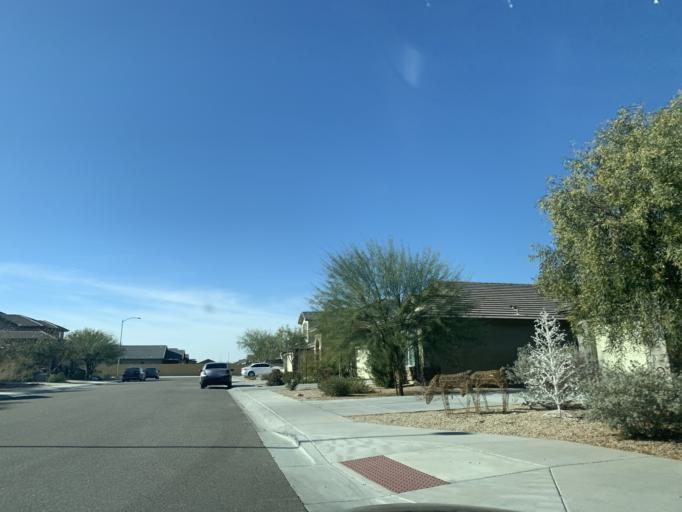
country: US
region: Arizona
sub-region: Maricopa County
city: Laveen
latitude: 33.3969
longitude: -112.1220
